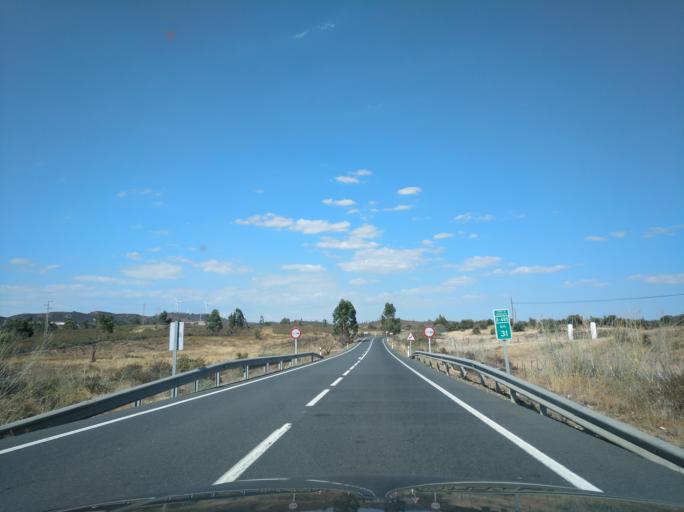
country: ES
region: Andalusia
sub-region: Provincia de Huelva
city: Alosno
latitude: 37.5666
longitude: -7.1220
